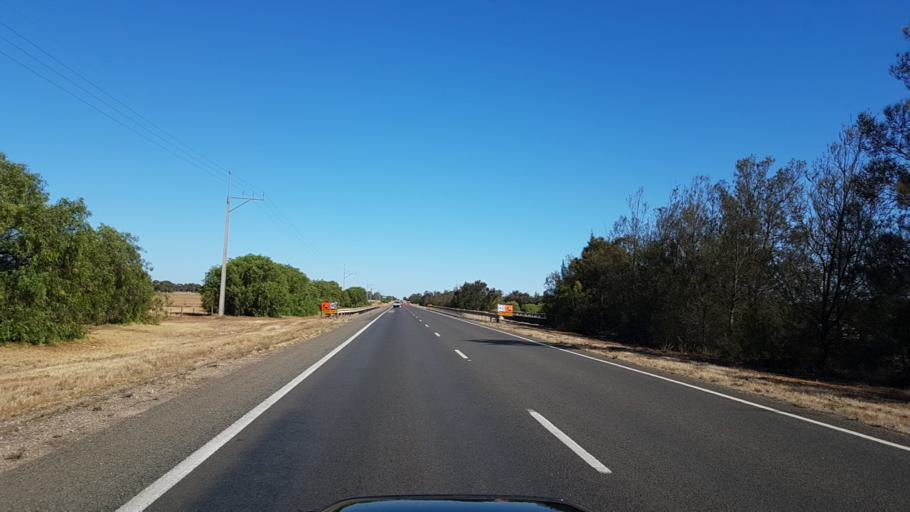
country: AU
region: South Australia
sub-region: Mallala
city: Two Wells
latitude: -34.5554
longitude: 138.4638
